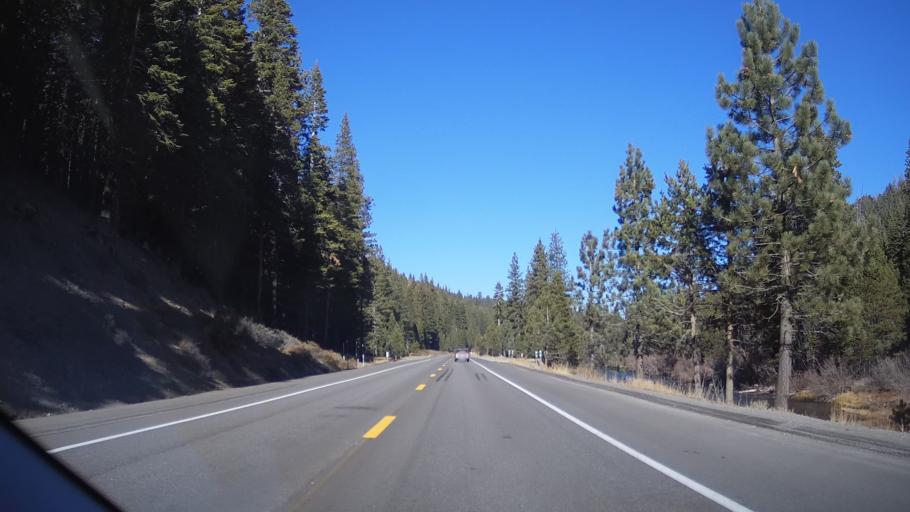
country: US
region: California
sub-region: Nevada County
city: Truckee
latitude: 39.2412
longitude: -120.2097
